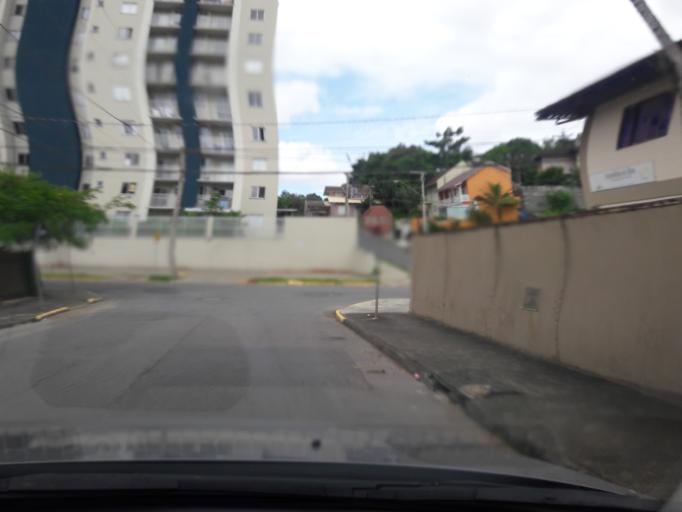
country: BR
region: Santa Catarina
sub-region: Joinville
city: Joinville
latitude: -26.3192
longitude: -48.8623
